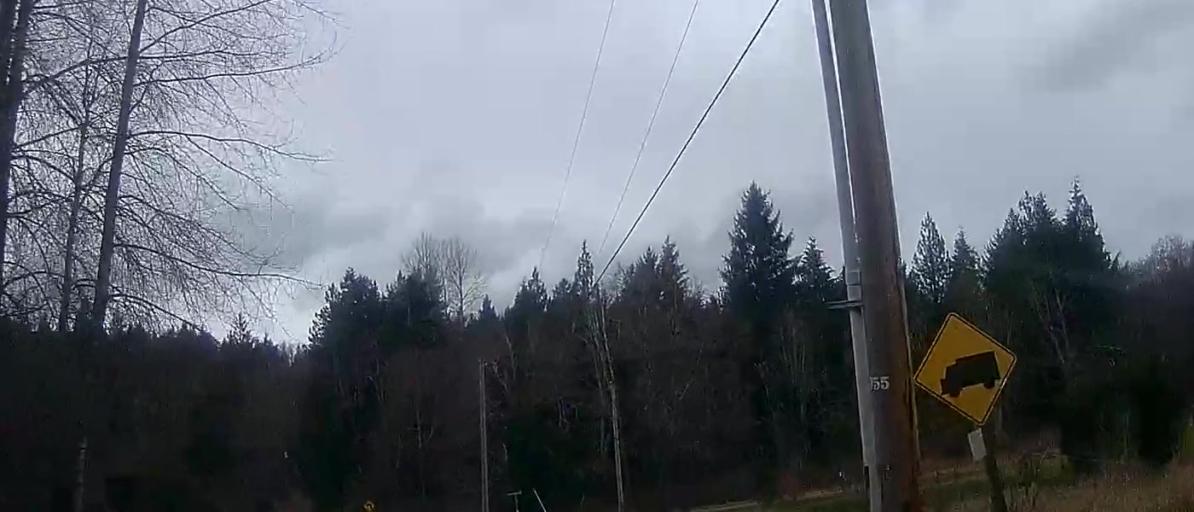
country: US
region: Washington
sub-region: Skagit County
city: Sedro-Woolley
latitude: 48.5870
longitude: -122.2391
